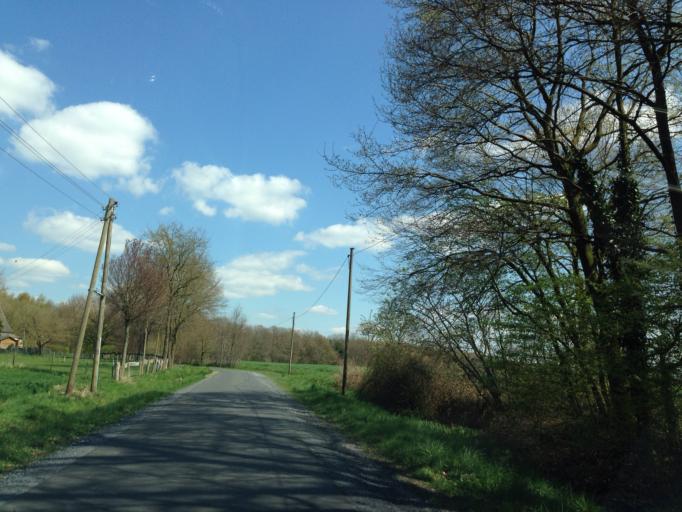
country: DE
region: North Rhine-Westphalia
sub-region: Regierungsbezirk Munster
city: Muenster
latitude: 51.9852
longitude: 7.5639
